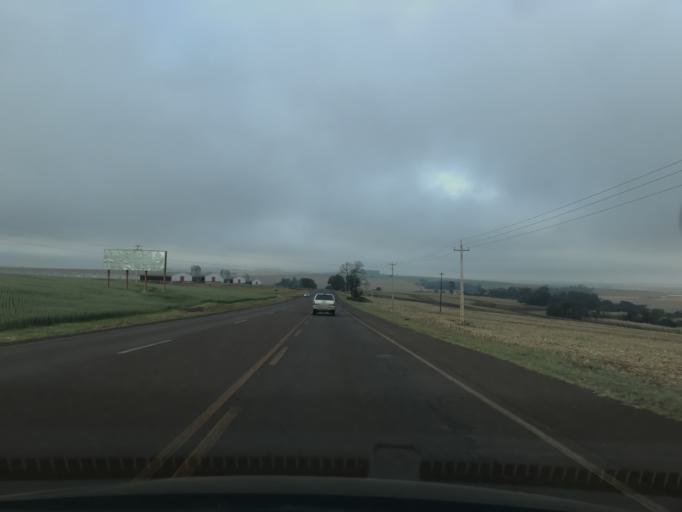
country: BR
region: Parana
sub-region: Toledo
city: Toledo
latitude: -24.6266
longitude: -53.7121
